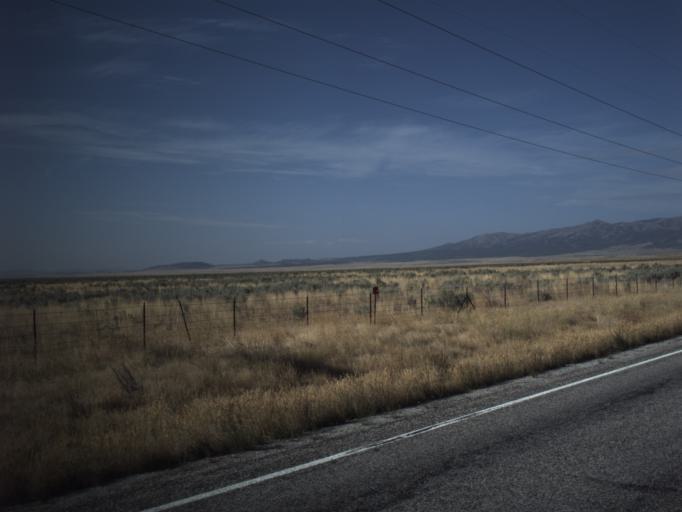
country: US
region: Idaho
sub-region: Oneida County
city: Malad City
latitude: 41.9656
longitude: -113.0236
